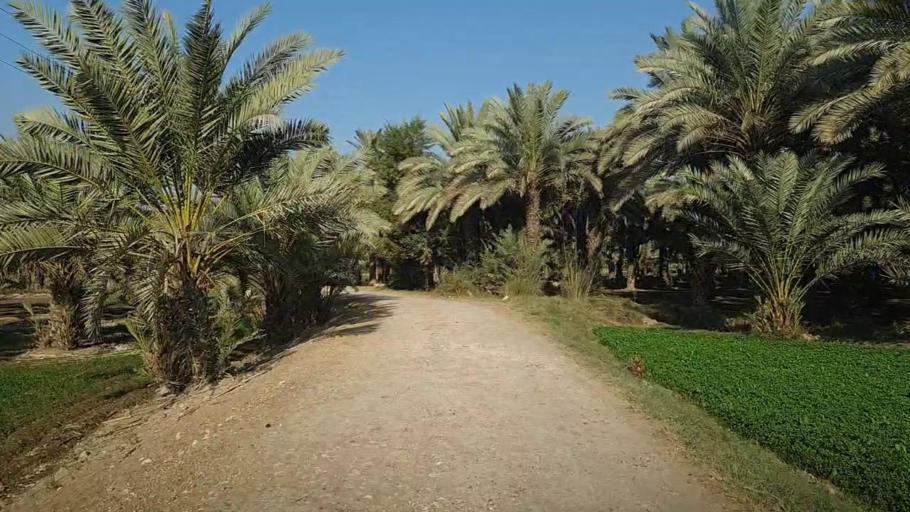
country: PK
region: Sindh
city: Ranipur
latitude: 27.2548
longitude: 68.5517
